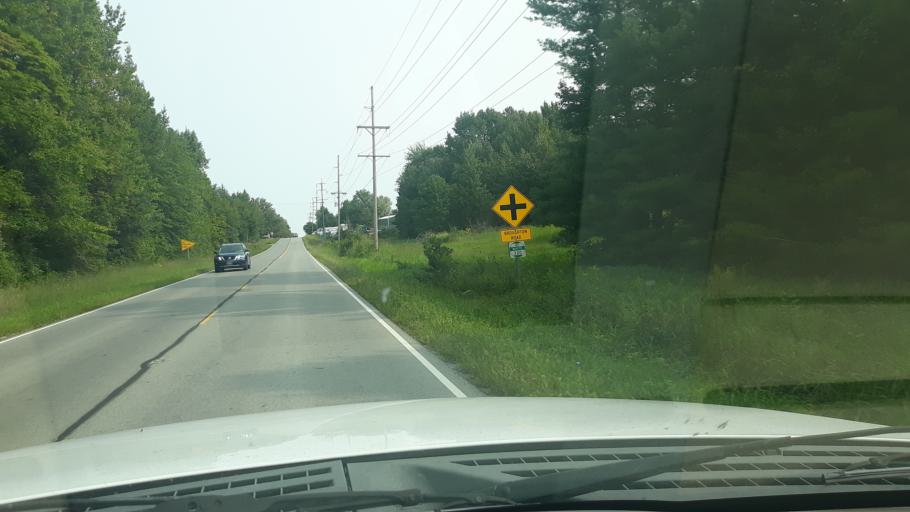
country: US
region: Illinois
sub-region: White County
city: Norris City
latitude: 37.9497
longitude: -88.3392
